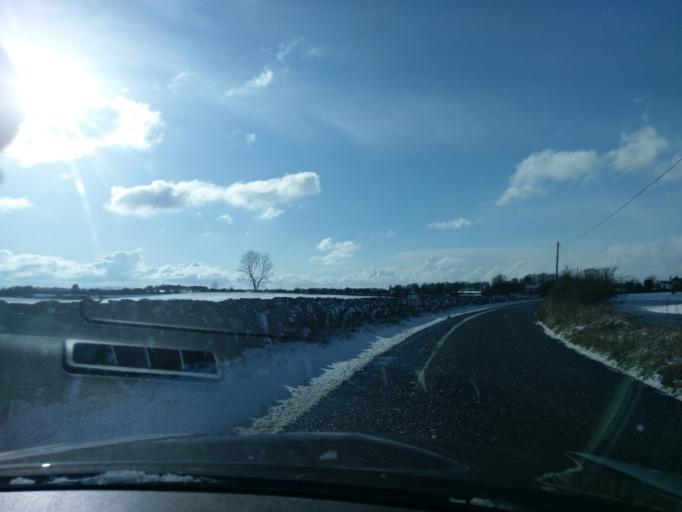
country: IE
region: Connaught
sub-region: County Galway
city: Athenry
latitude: 53.2035
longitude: -8.7695
